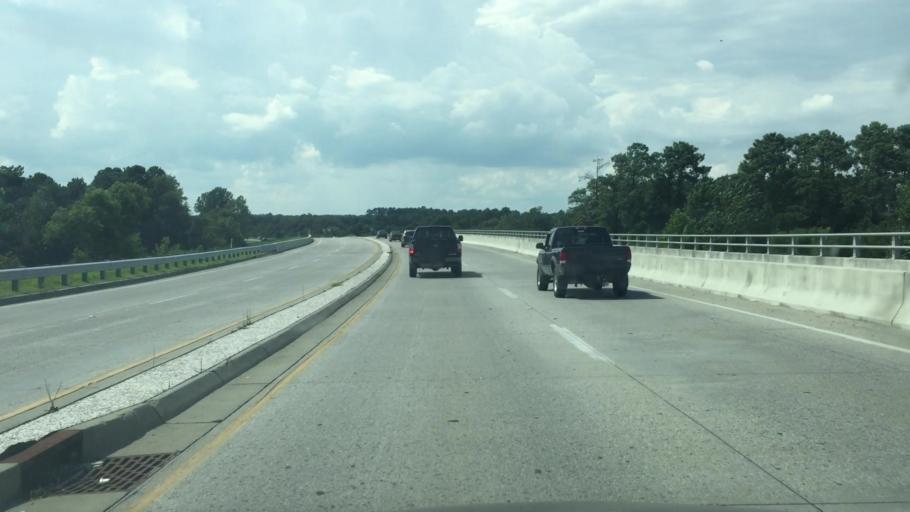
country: US
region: South Carolina
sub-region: Horry County
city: North Myrtle Beach
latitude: 33.8356
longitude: -78.6859
